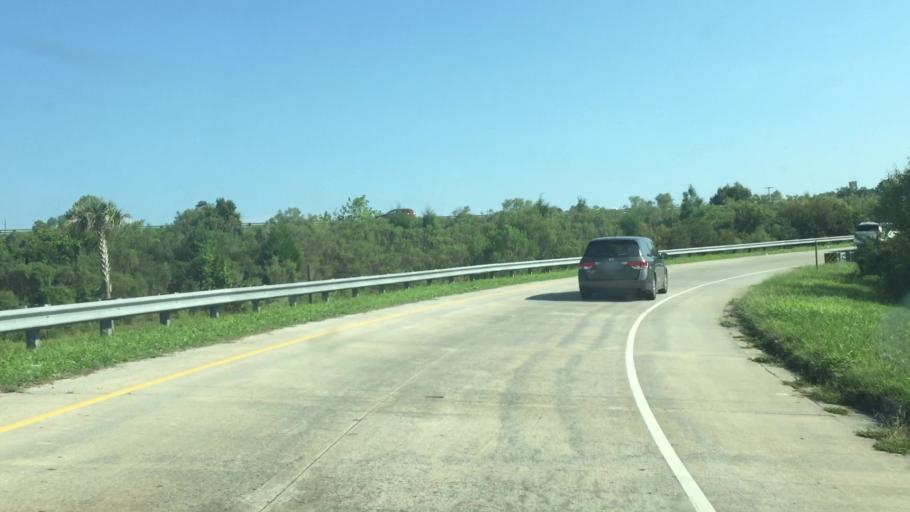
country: US
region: South Carolina
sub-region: Horry County
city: North Myrtle Beach
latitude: 33.7864
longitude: -78.7739
